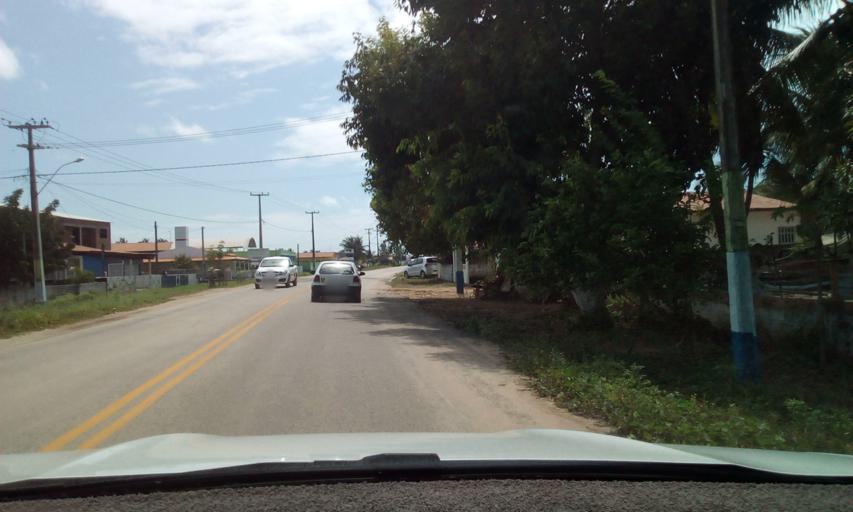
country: BR
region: Paraiba
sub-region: Rio Tinto
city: Rio Tinto
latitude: -6.6993
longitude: -34.9363
